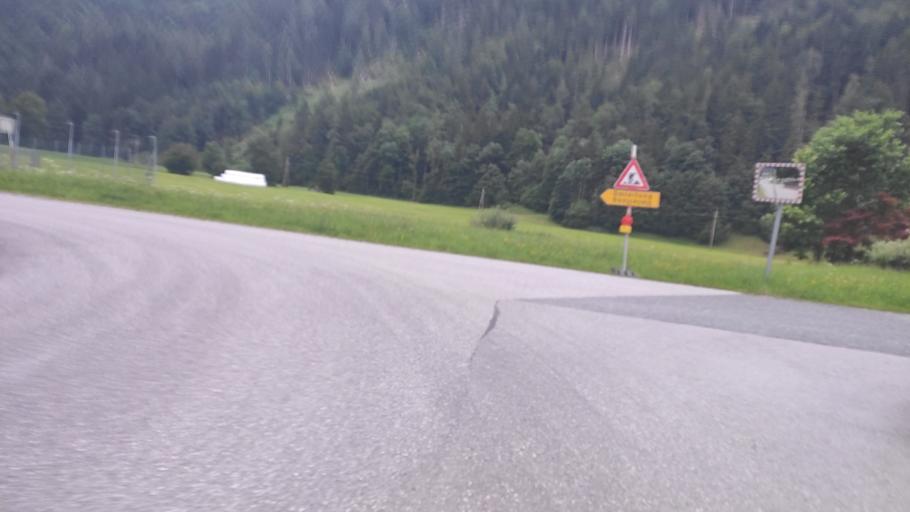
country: AT
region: Salzburg
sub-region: Politischer Bezirk Zell am See
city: Sankt Martin bei Lofer
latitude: 47.5729
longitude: 12.6936
